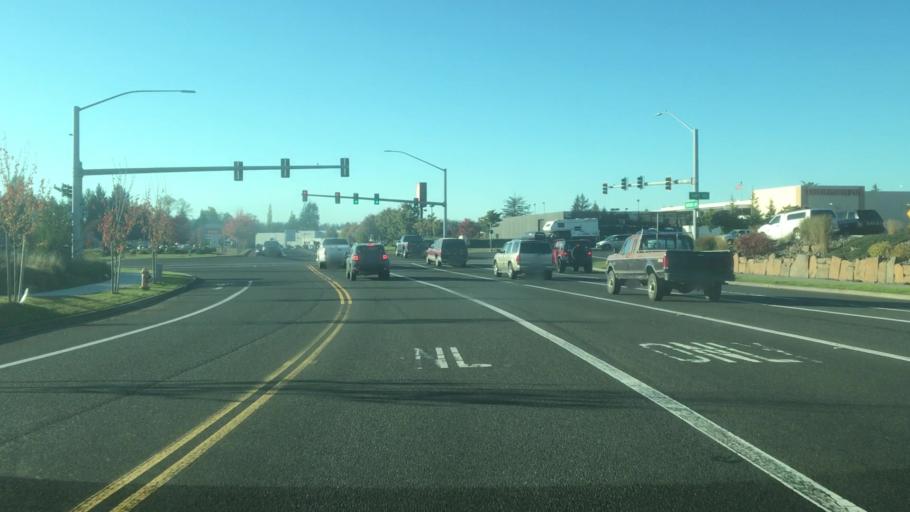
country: US
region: Oregon
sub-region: Clatsop County
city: Warrenton
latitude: 46.1468
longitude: -123.9167
